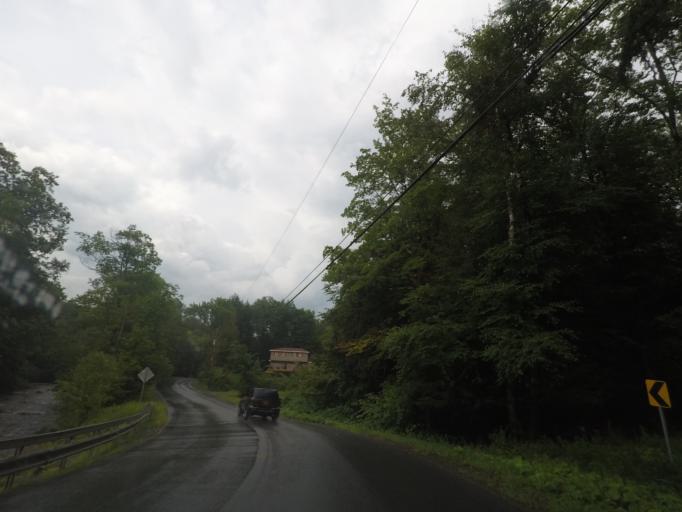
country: US
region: New York
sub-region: Rensselaer County
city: Poestenkill
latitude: 42.6767
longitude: -73.5361
